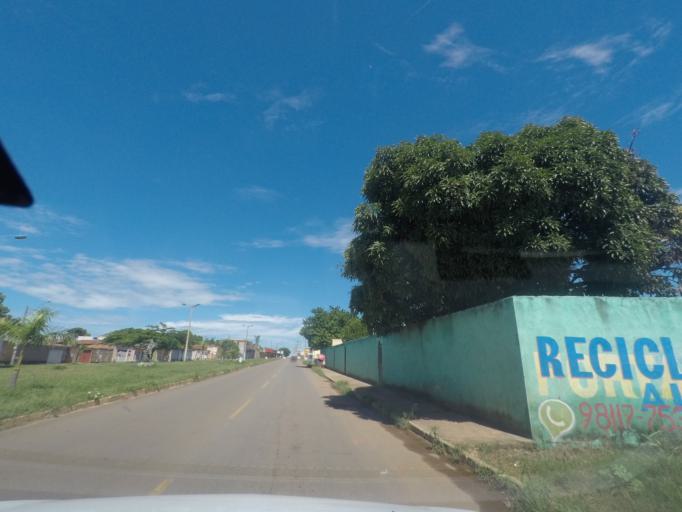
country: BR
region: Goias
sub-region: Aparecida De Goiania
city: Aparecida de Goiania
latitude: -16.8040
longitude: -49.3242
